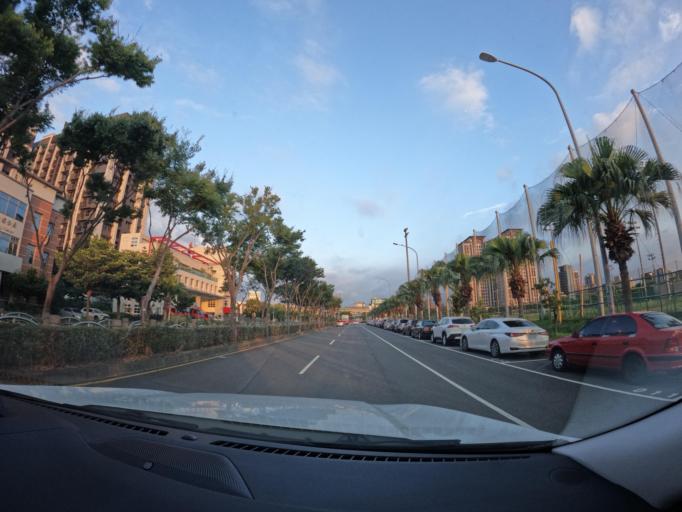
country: TW
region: Taiwan
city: Taoyuan City
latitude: 25.0138
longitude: 121.2102
